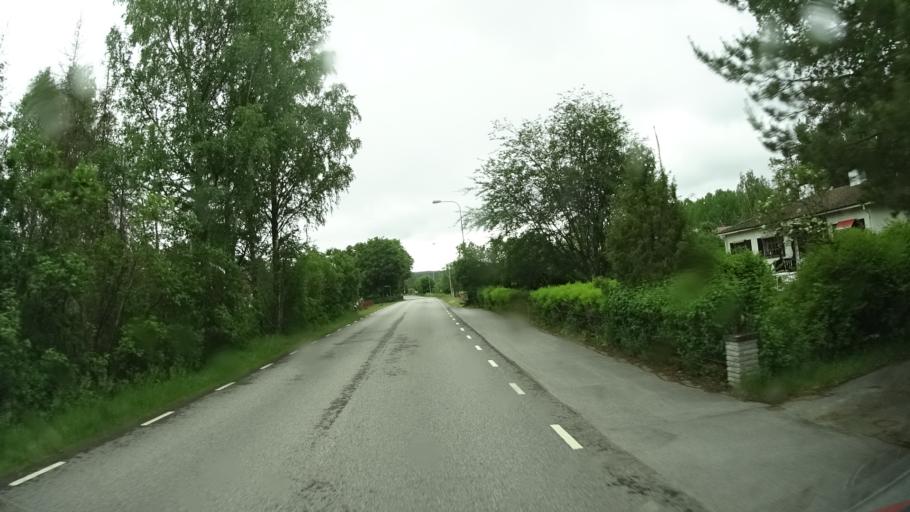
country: SE
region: Joenkoeping
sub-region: Eksjo Kommun
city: Mariannelund
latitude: 57.6923
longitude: 15.6245
